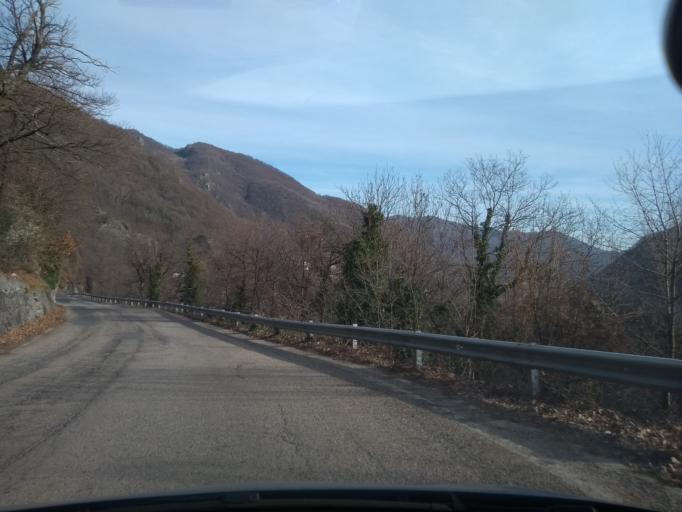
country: IT
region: Piedmont
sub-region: Provincia di Torino
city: Ala di Stura
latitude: 45.3208
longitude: 7.3408
